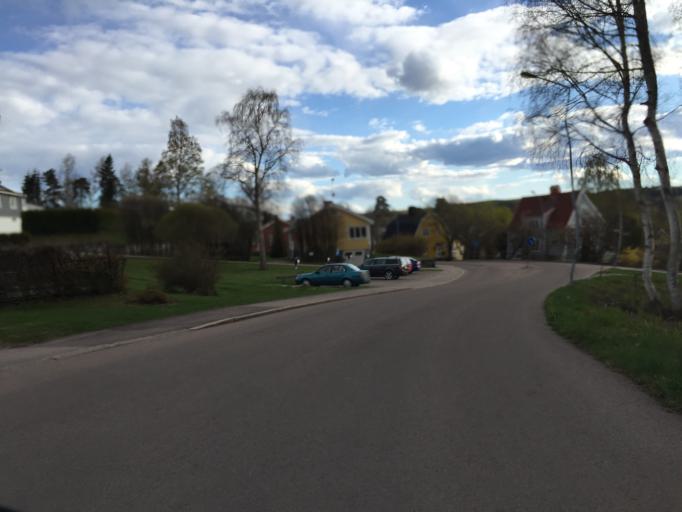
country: SE
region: Dalarna
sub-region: Ludvika Kommun
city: Ludvika
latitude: 60.1388
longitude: 15.1812
